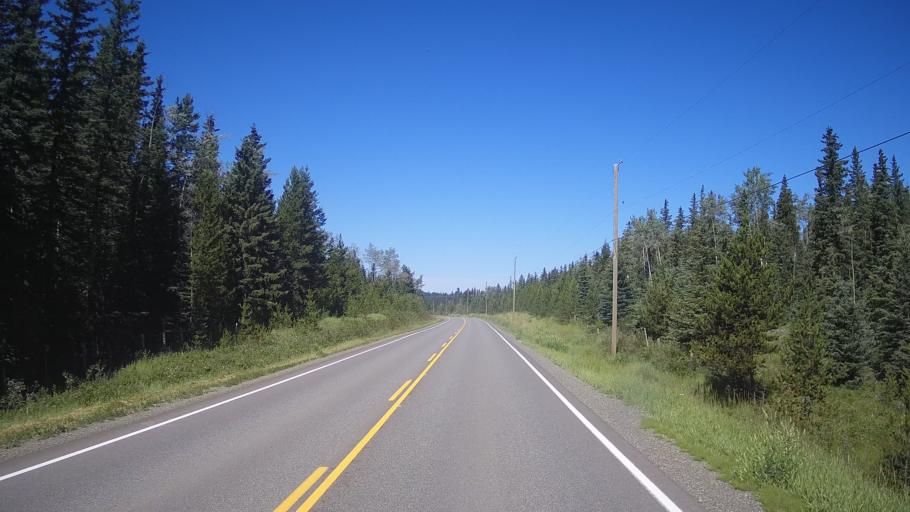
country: CA
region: British Columbia
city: Cache Creek
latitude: 51.5451
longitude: -121.0679
